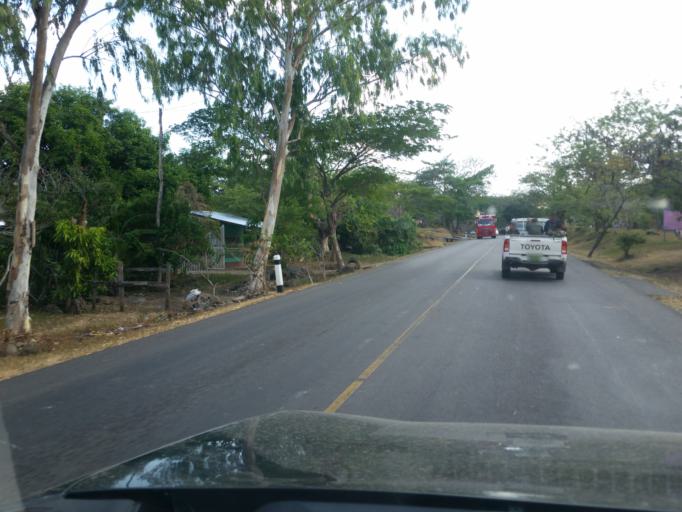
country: NI
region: Chontales
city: Comalapa
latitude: 12.1927
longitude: -85.6162
